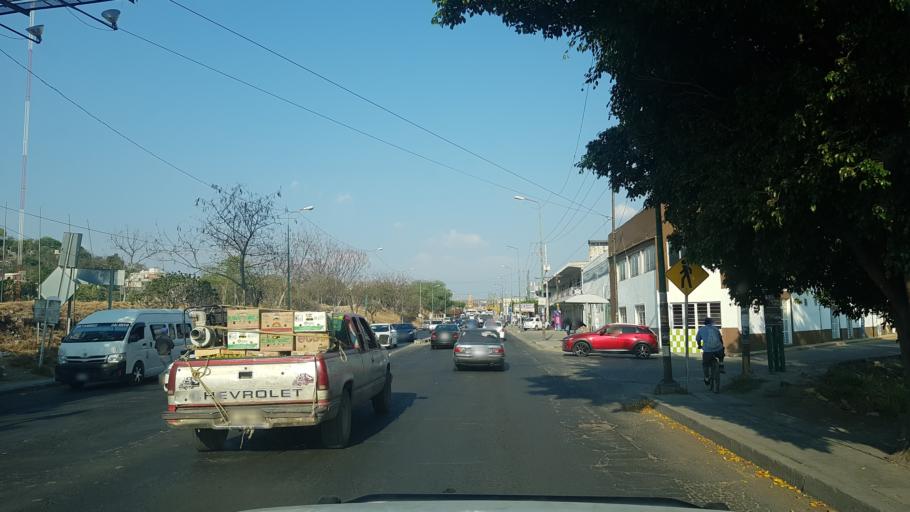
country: MX
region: Puebla
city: Izucar de Matamoros
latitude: 18.6008
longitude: -98.4756
